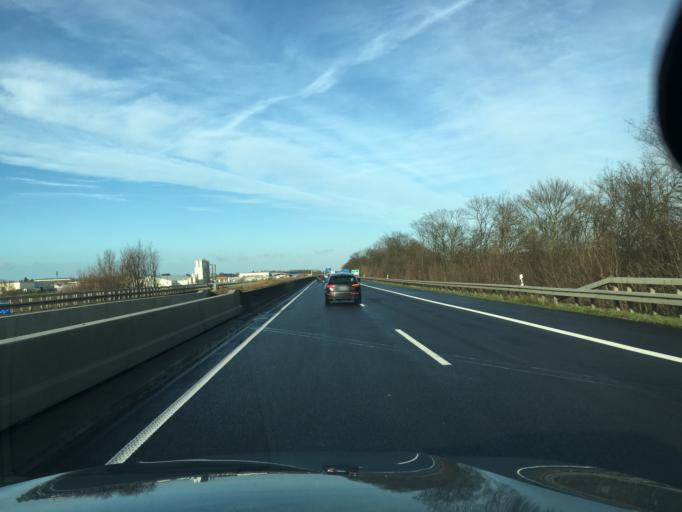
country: DE
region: North Rhine-Westphalia
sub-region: Regierungsbezirk Koln
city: Weilerswist
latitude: 50.7481
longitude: 6.8621
